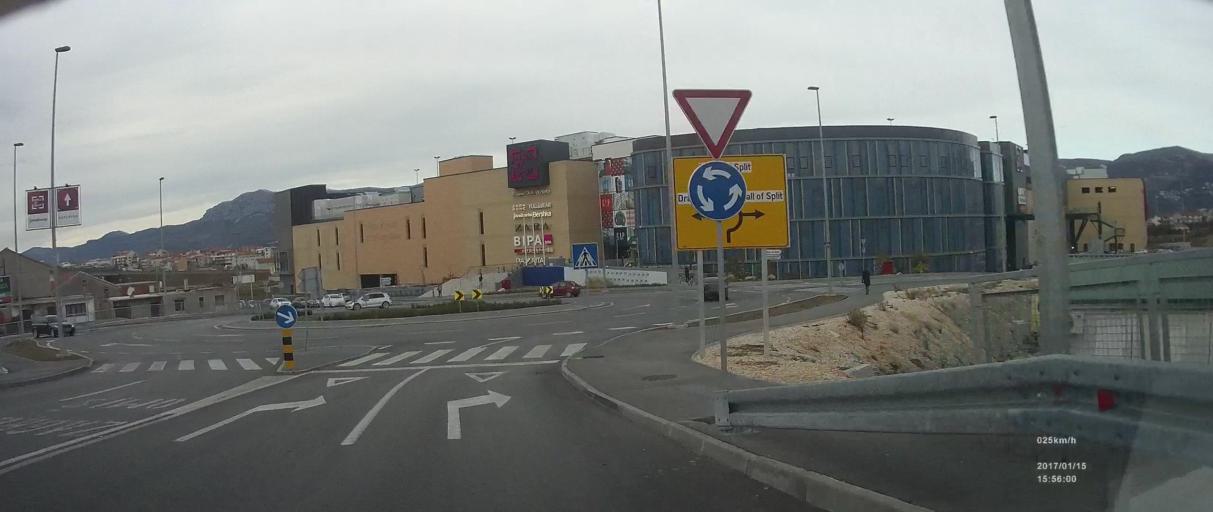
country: HR
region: Splitsko-Dalmatinska
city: Vranjic
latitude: 43.5173
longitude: 16.4842
